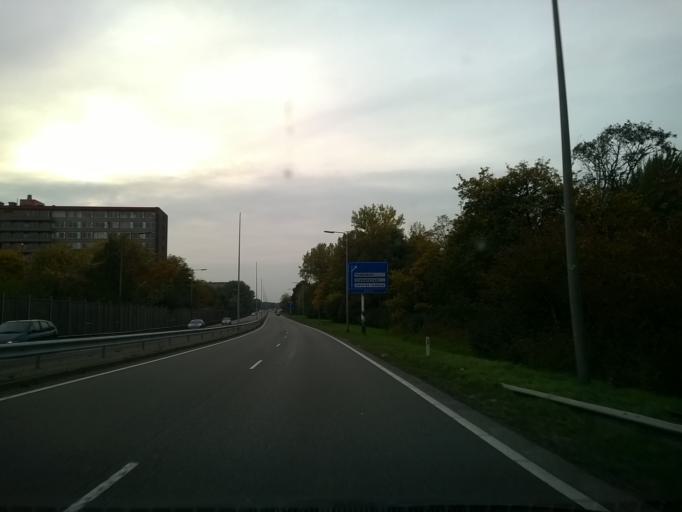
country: NL
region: Groningen
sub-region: Gemeente Groningen
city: Korrewegwijk
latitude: 53.2383
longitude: 6.5518
